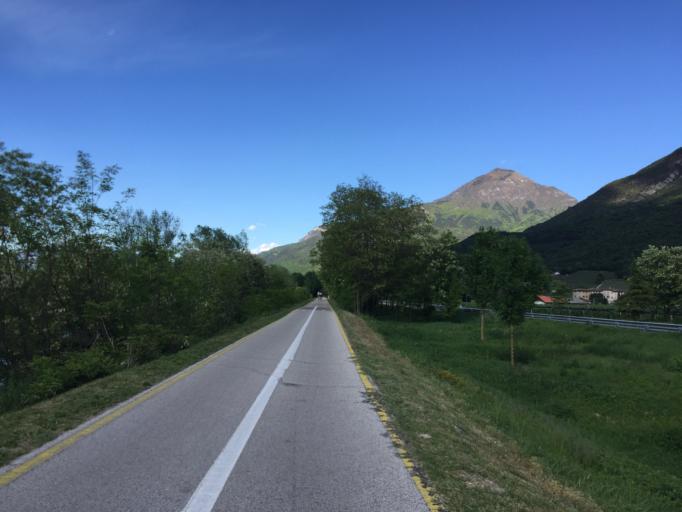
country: IT
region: Trentino-Alto Adige
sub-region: Provincia di Trento
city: Aldeno
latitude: 45.9855
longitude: 11.1139
